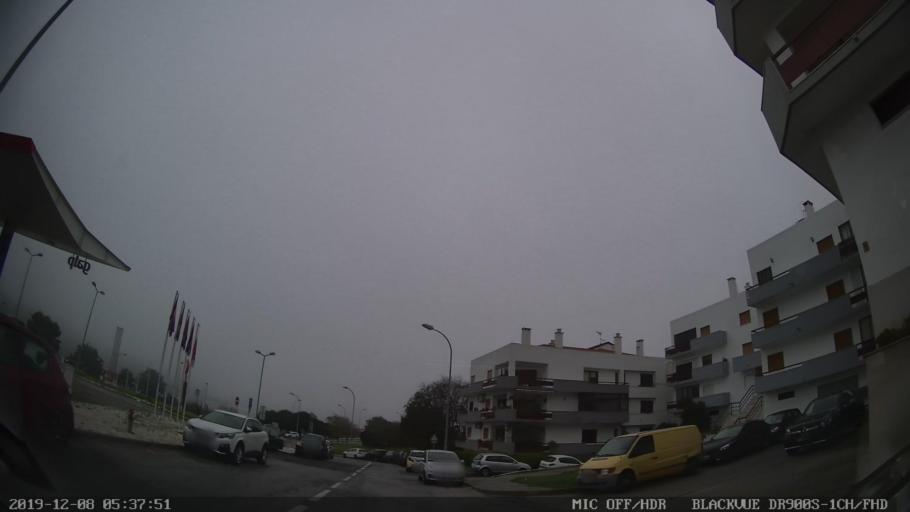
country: PT
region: Lisbon
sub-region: Oeiras
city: Alges
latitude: 38.7221
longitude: -9.2191
